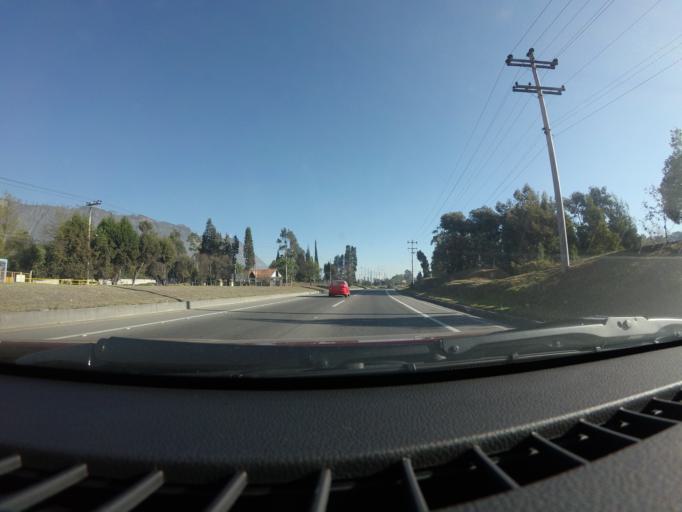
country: CO
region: Cundinamarca
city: Cajica
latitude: 4.9565
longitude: -74.0112
